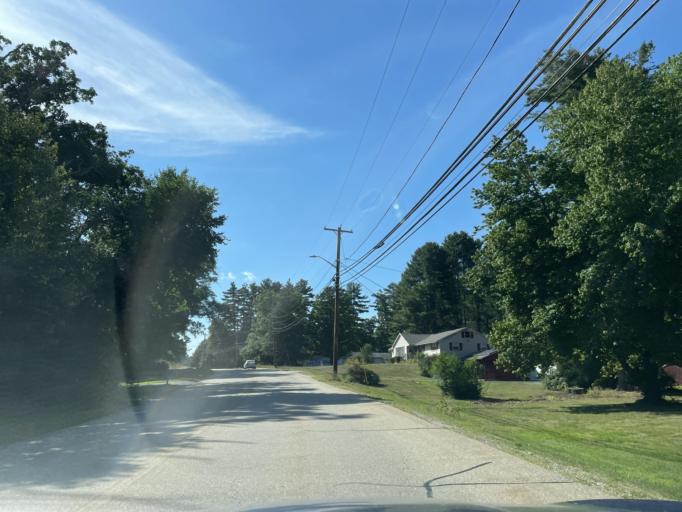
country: US
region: Massachusetts
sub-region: Worcester County
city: Oxford
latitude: 42.1151
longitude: -71.8829
